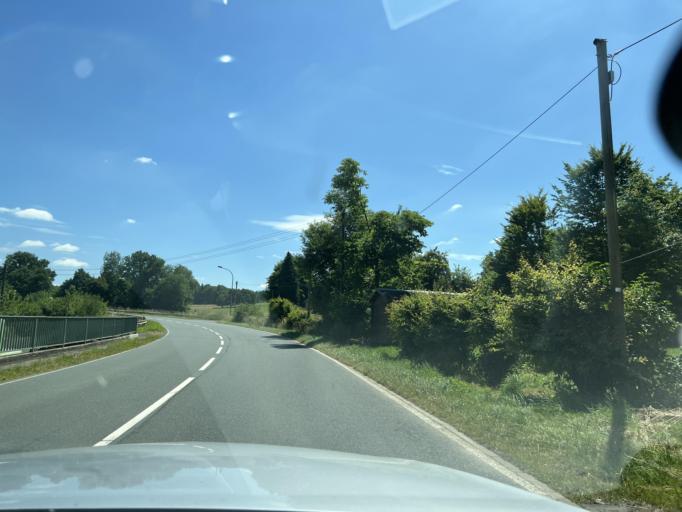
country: DE
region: North Rhine-Westphalia
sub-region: Regierungsbezirk Arnsberg
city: Wenden
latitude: 50.9656
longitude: 7.9097
